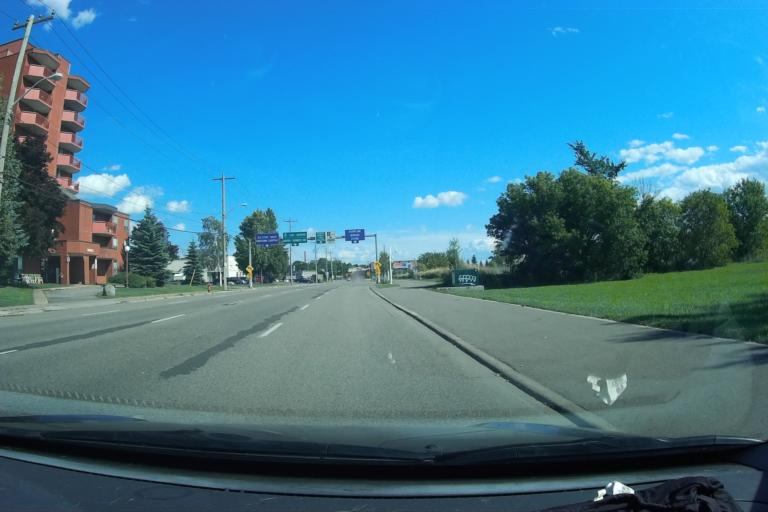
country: CA
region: Ontario
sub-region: Algoma
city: Sault Ste. Marie
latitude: 46.5065
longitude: -84.3283
